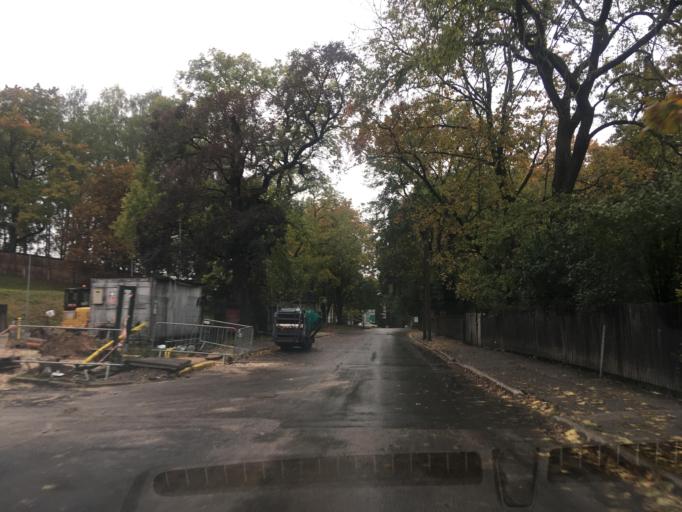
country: EE
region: Tartu
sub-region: Tartu linn
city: Tartu
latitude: 58.3873
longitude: 26.7056
